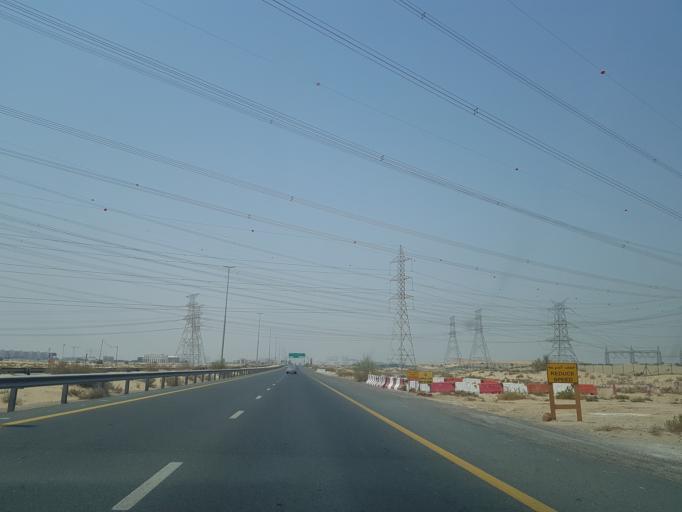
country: AE
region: Ash Shariqah
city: Sharjah
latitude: 25.1437
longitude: 55.4333
